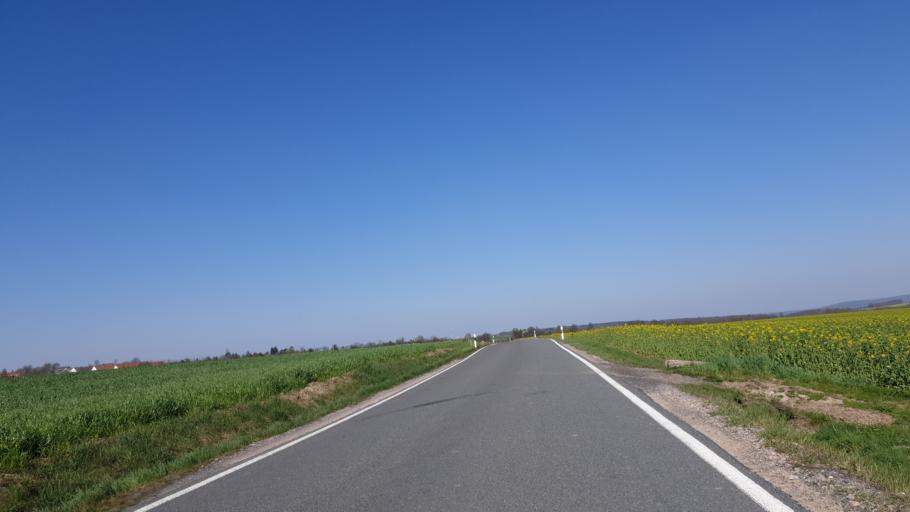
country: DE
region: Saxony
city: Taura
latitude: 50.9251
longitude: 12.8336
